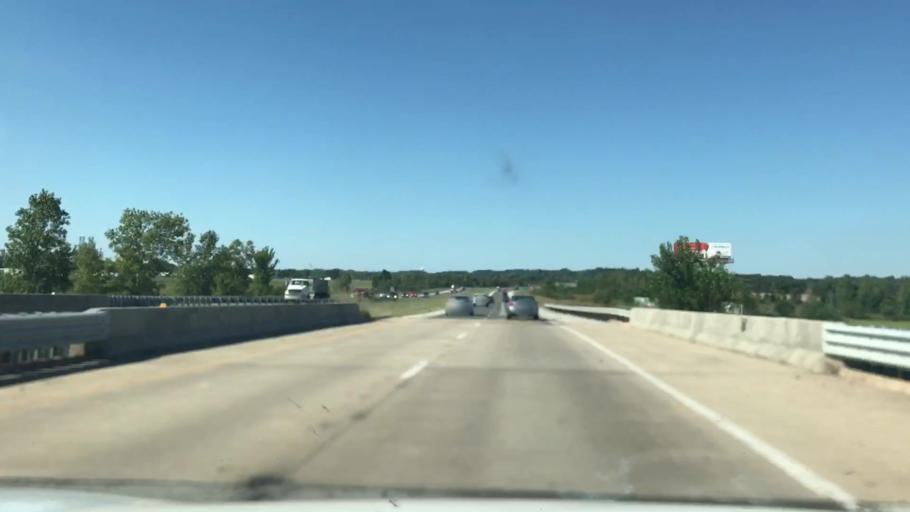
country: US
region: Illinois
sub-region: Madison County
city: South Roxana
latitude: 38.8201
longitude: -90.0423
